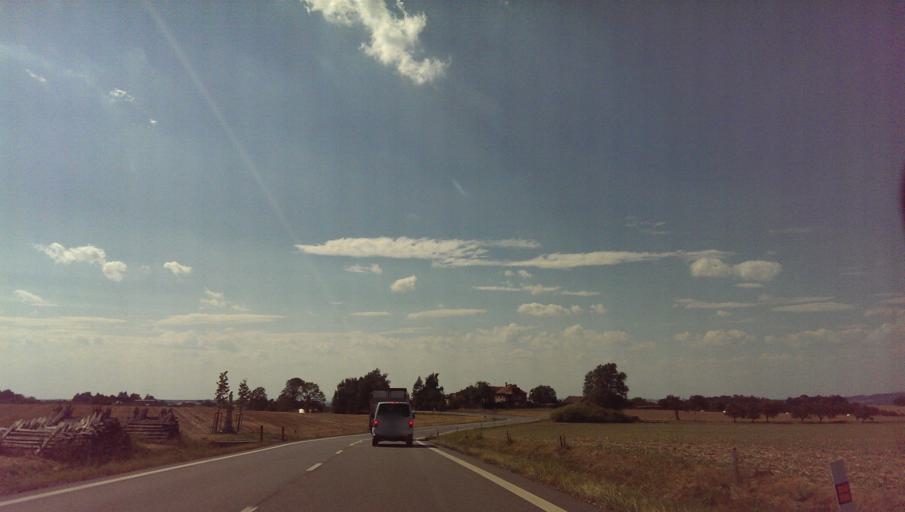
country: CZ
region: Zlin
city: Chvalcov
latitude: 49.4322
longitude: 17.7592
